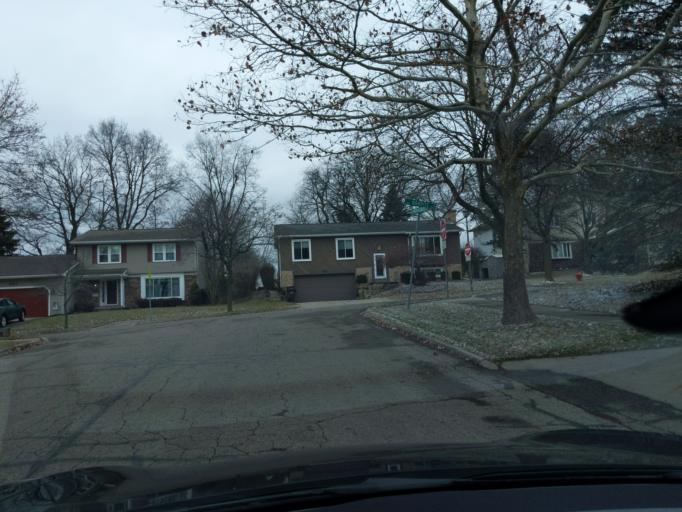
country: US
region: Michigan
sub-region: Ingham County
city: East Lansing
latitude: 42.7582
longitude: -84.5189
